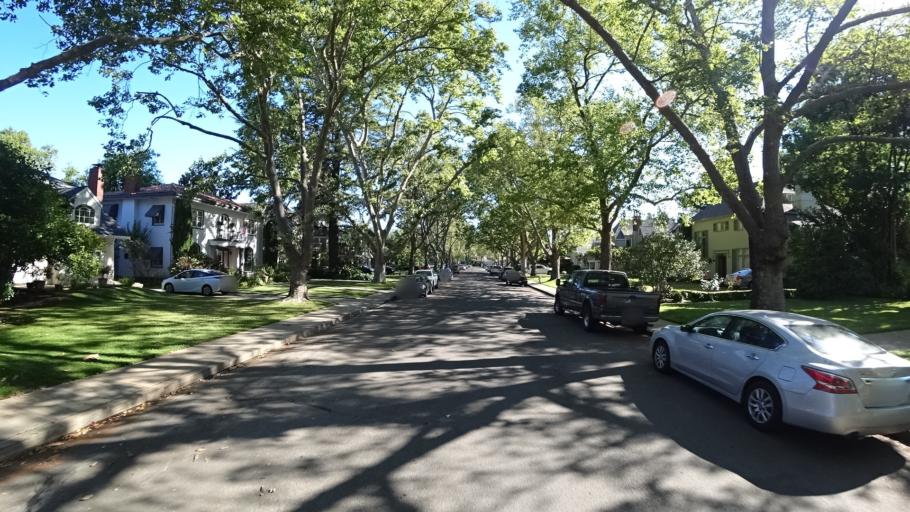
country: US
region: California
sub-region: Sacramento County
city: Sacramento
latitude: 38.5669
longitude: -121.4503
